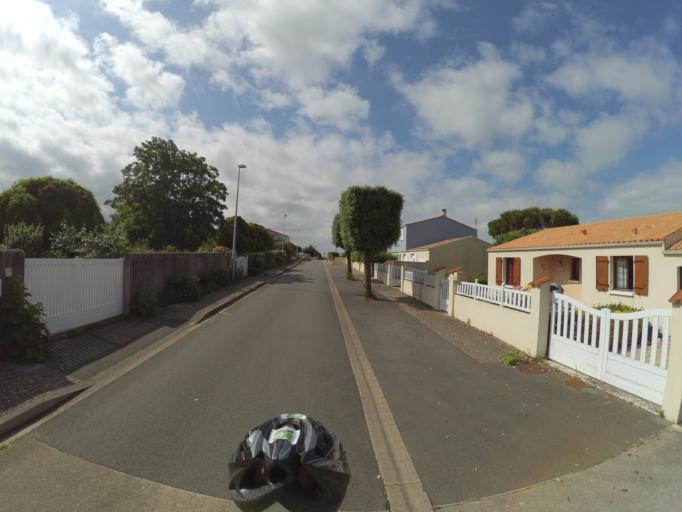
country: FR
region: Poitou-Charentes
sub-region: Departement de la Charente-Maritime
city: Angoulins
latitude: 46.1041
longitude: -1.1184
